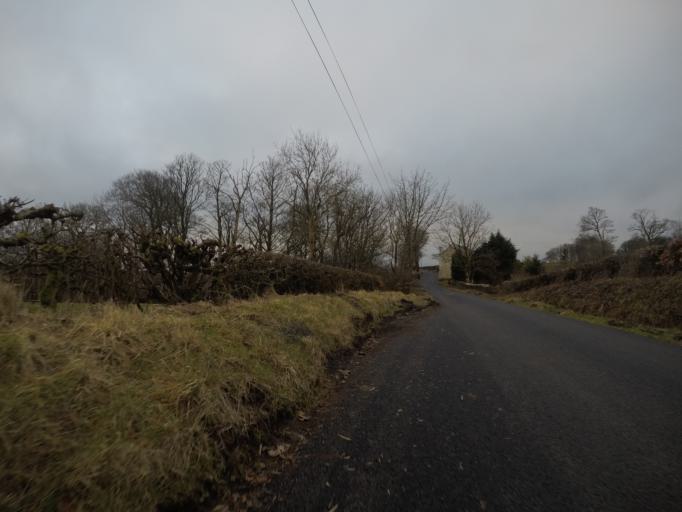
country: GB
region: Scotland
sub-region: North Ayrshire
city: Dalry
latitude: 55.7157
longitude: -4.7527
